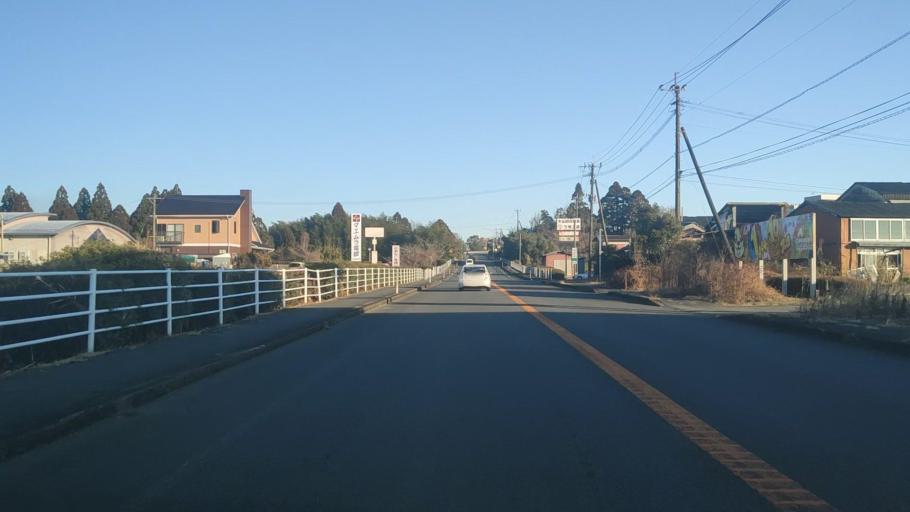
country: JP
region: Miyazaki
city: Takanabe
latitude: 32.1896
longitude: 131.5239
